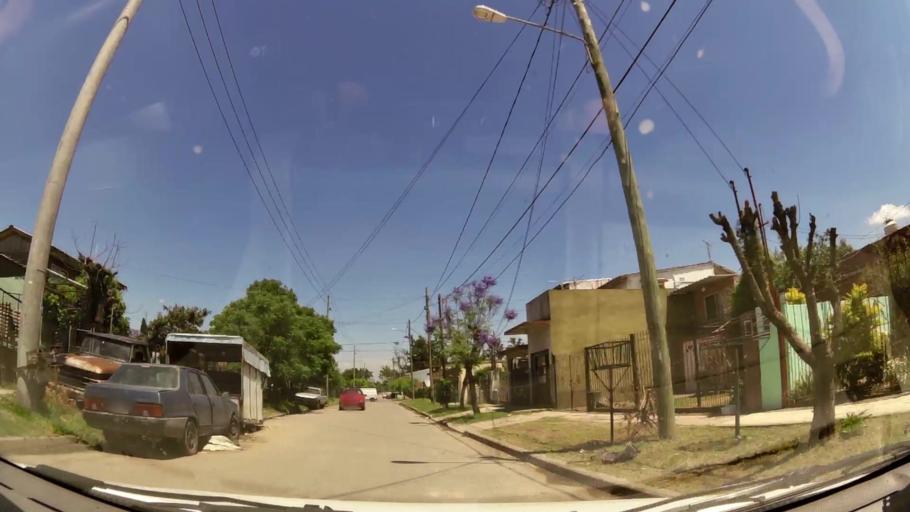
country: AR
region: Buenos Aires
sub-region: Partido de Merlo
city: Merlo
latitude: -34.6427
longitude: -58.7133
